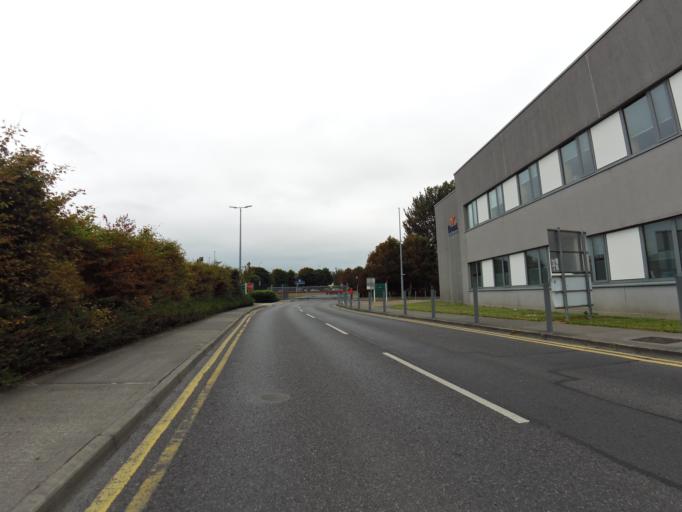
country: IE
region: Connaught
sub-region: County Galway
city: Gaillimh
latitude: 53.2782
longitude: -9.0687
